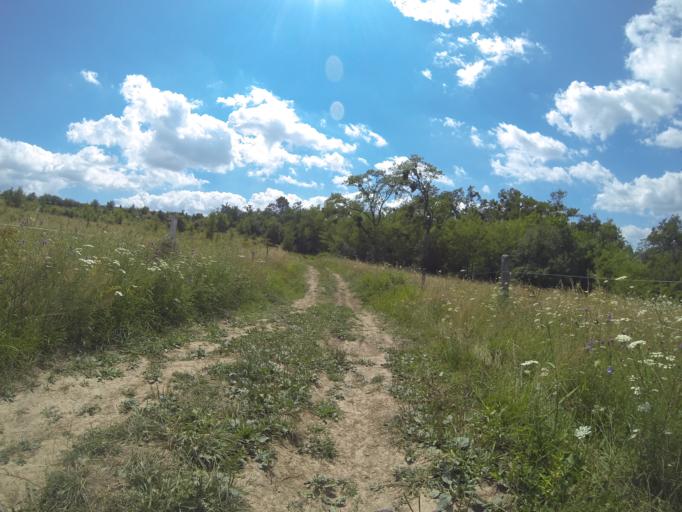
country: RO
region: Brasov
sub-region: Comuna Sercaia
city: Sercaia
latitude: 45.8654
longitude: 25.0897
